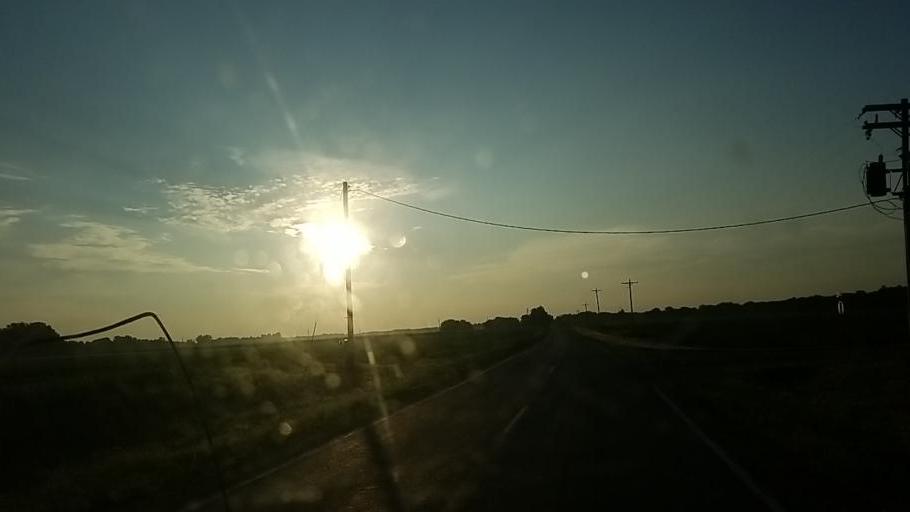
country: US
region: Michigan
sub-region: Montcalm County
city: Howard City
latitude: 43.3591
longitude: -85.3834
